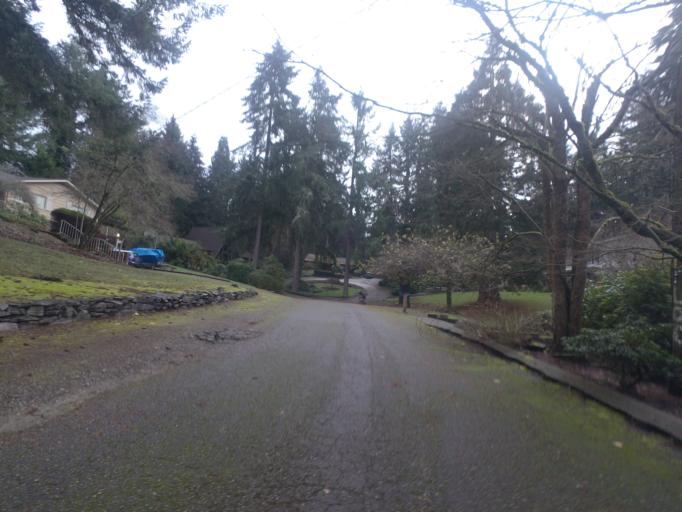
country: US
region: Washington
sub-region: Pierce County
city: University Place
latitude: 47.2237
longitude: -122.5473
